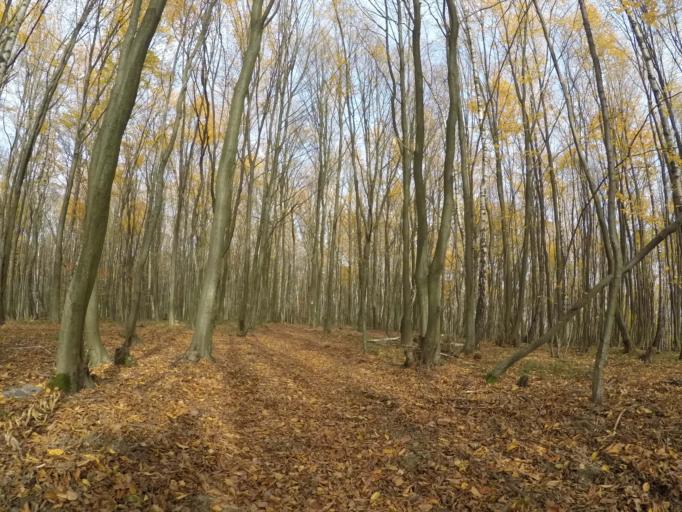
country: SK
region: Presovsky
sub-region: Okres Presov
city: Presov
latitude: 48.9242
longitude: 21.2202
